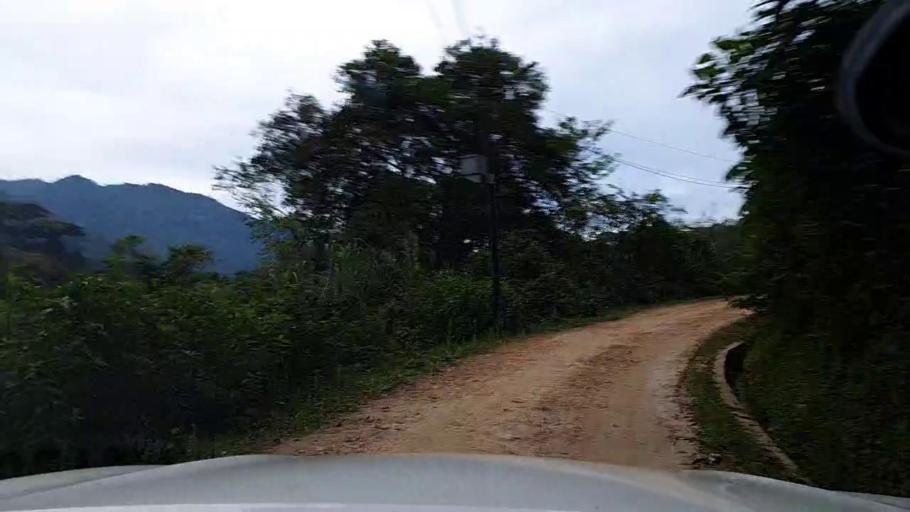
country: RW
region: Western Province
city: Cyangugu
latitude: -2.5648
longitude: 29.2314
